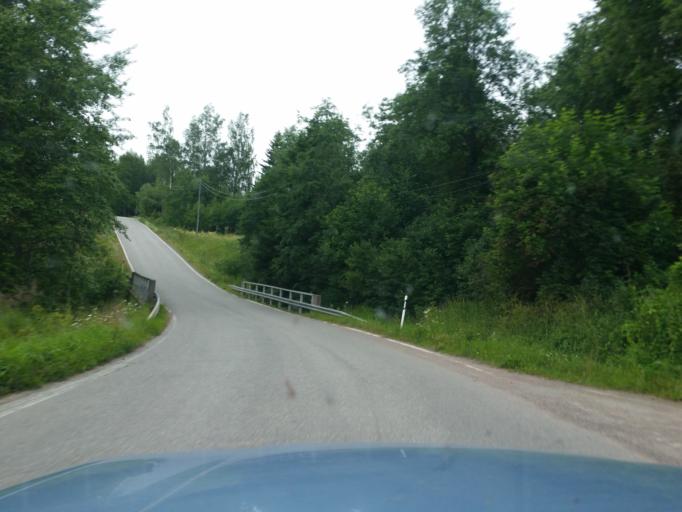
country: FI
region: Uusimaa
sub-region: Helsinki
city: Sammatti
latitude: 60.4705
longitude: 23.8409
